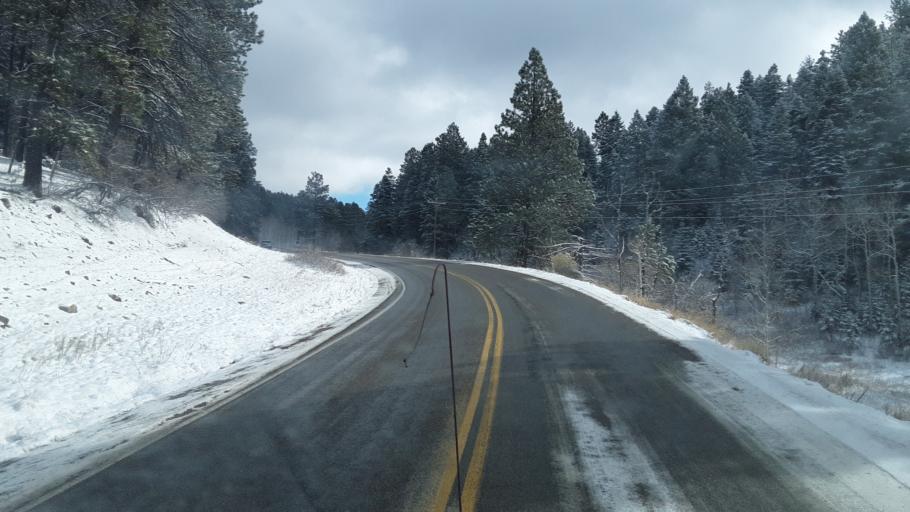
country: US
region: Colorado
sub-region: La Plata County
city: Bayfield
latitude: 37.3577
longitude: -107.6670
